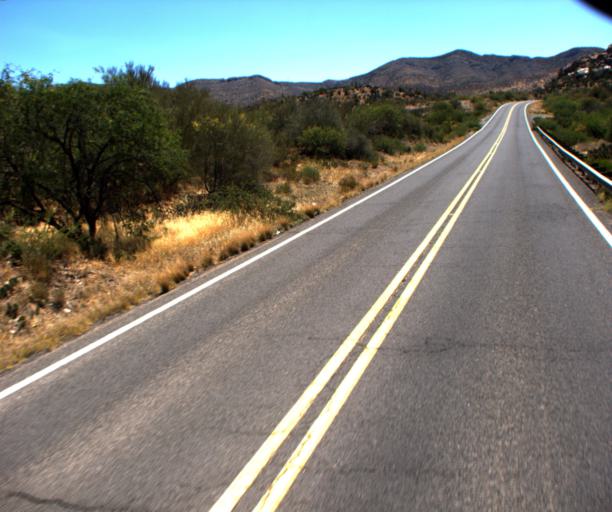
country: US
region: Arizona
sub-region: Pinal County
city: Superior
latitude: 33.2262
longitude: -111.0803
